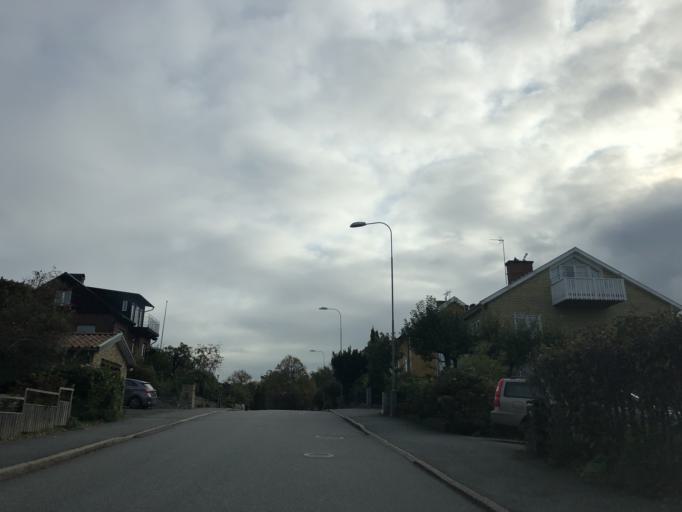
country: SE
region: Vaestra Goetaland
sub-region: Goteborg
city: Majorna
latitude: 57.6765
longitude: 11.8749
